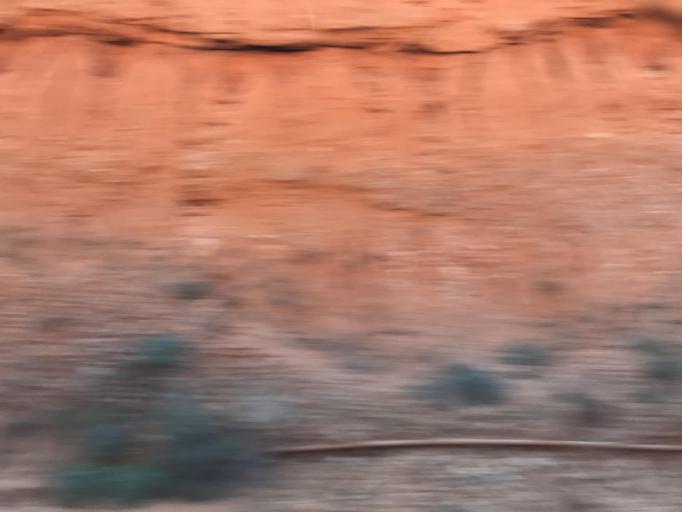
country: ES
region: Castille and Leon
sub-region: Provincia de Soria
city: Arcos de Jalon
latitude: 41.1717
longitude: -2.2616
